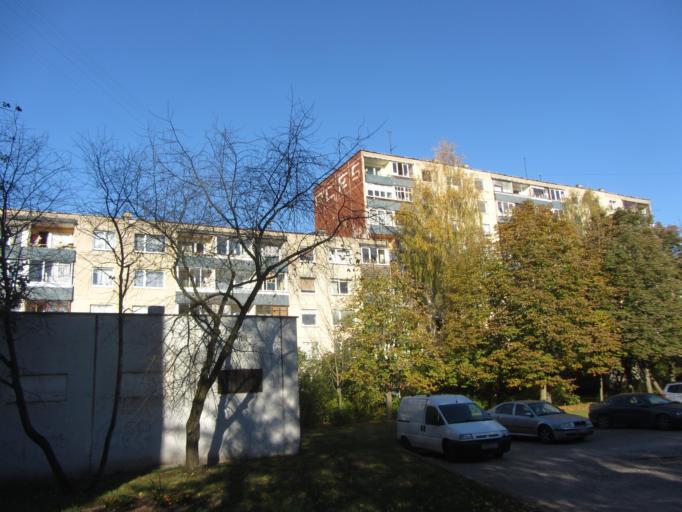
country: LT
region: Vilnius County
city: Lazdynai
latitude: 54.6896
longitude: 25.2147
